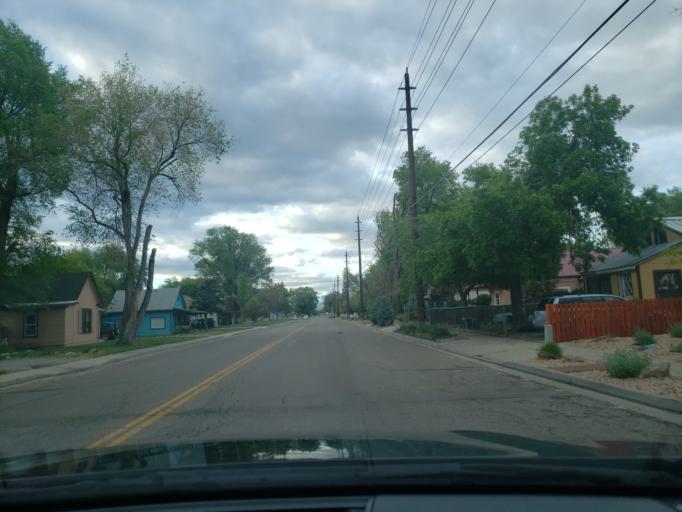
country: US
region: Colorado
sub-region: Mesa County
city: Fruita
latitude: 39.1574
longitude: -108.7290
